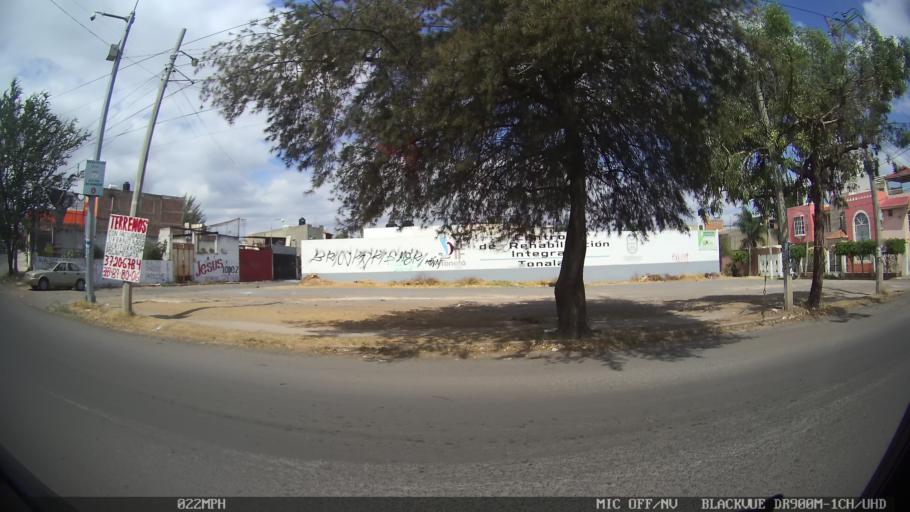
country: MX
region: Jalisco
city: Tonala
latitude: 20.6319
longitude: -103.2501
